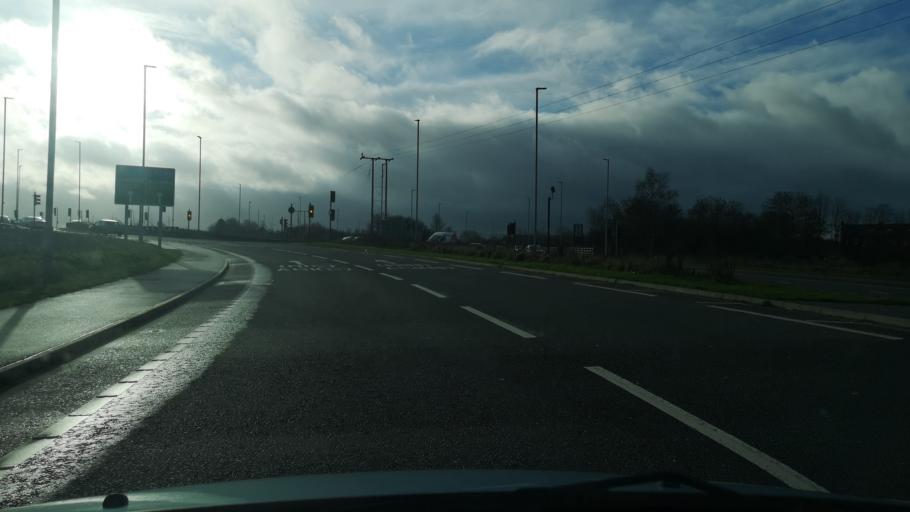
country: GB
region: England
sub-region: Barnsley
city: Birdwell
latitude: 53.5003
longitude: -1.4735
